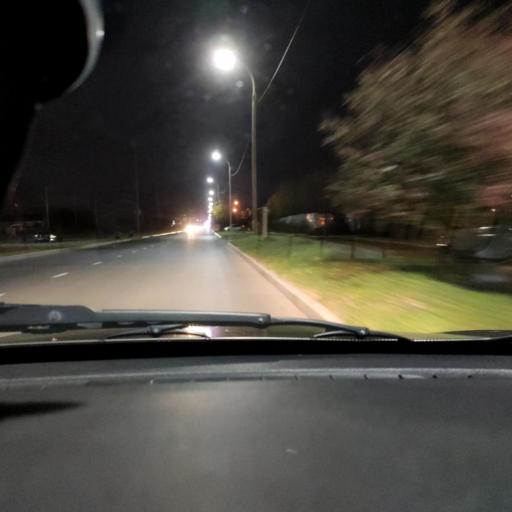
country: RU
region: Samara
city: Tol'yatti
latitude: 53.5163
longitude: 49.3956
